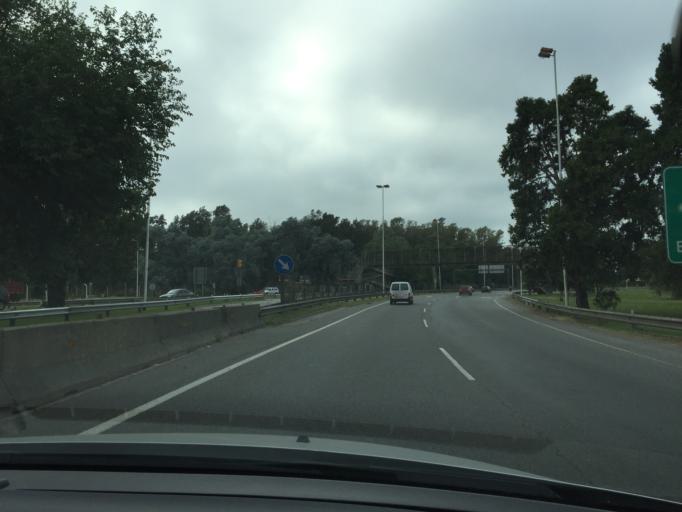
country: AR
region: Buenos Aires
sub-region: Partido de Ezeiza
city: Ezeiza
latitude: -34.7844
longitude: -58.5227
